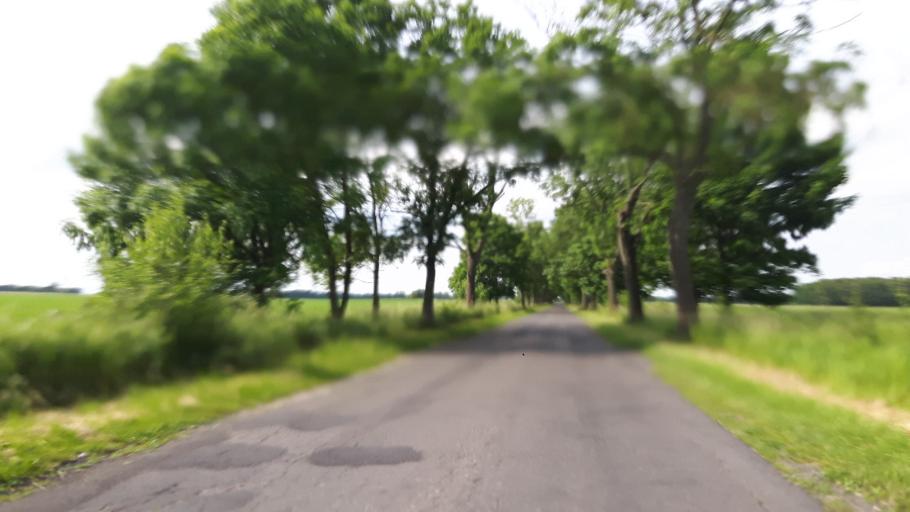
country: PL
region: West Pomeranian Voivodeship
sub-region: Powiat goleniowski
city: Nowogard
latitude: 53.7457
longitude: 15.1162
